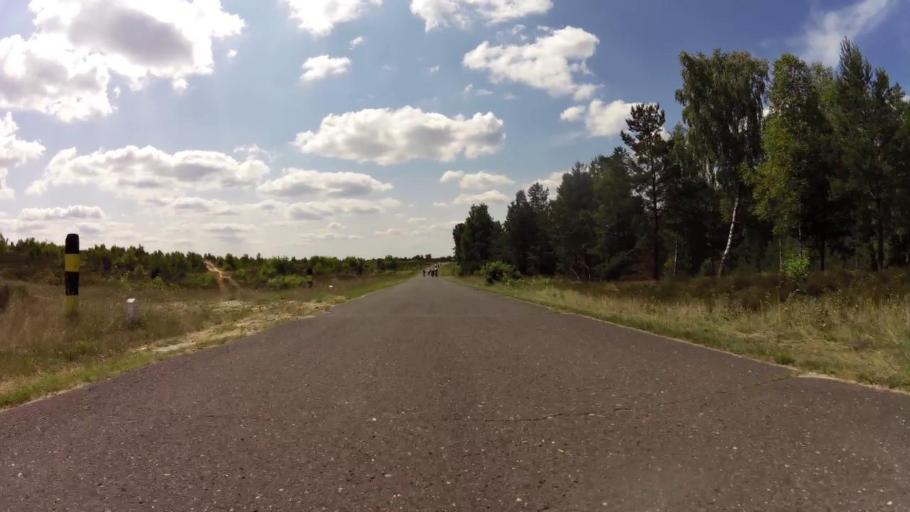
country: PL
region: West Pomeranian Voivodeship
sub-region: Powiat drawski
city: Drawsko Pomorskie
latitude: 53.4311
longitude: 15.7499
